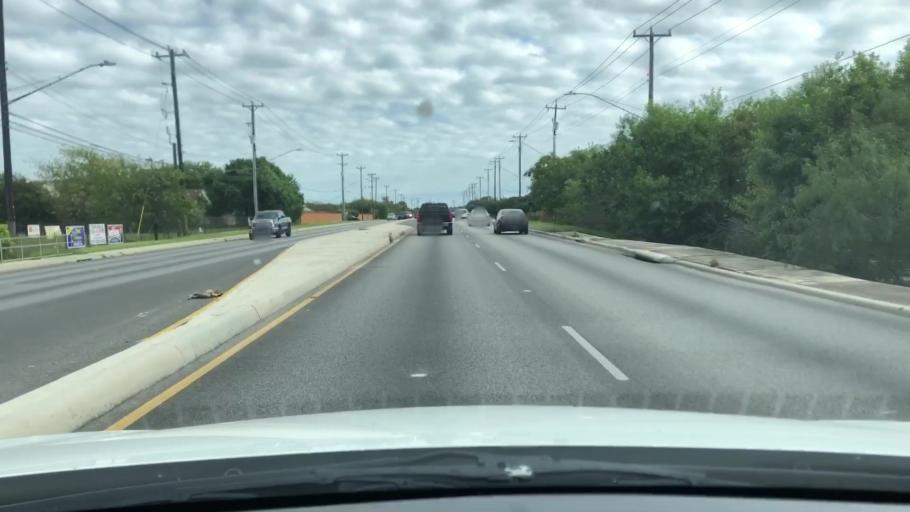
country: US
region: Texas
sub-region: Bexar County
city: Leon Valley
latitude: 29.4888
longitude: -98.6765
